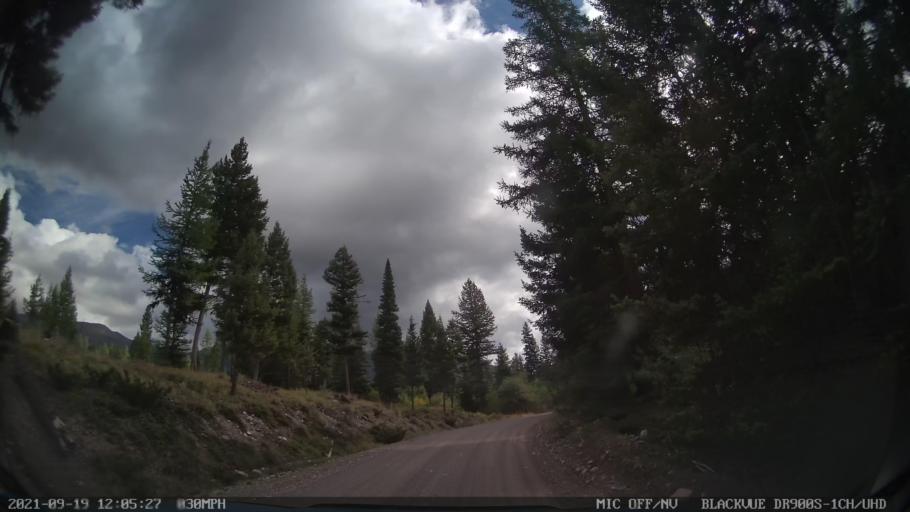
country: US
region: Montana
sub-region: Missoula County
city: Seeley Lake
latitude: 47.1910
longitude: -113.4252
